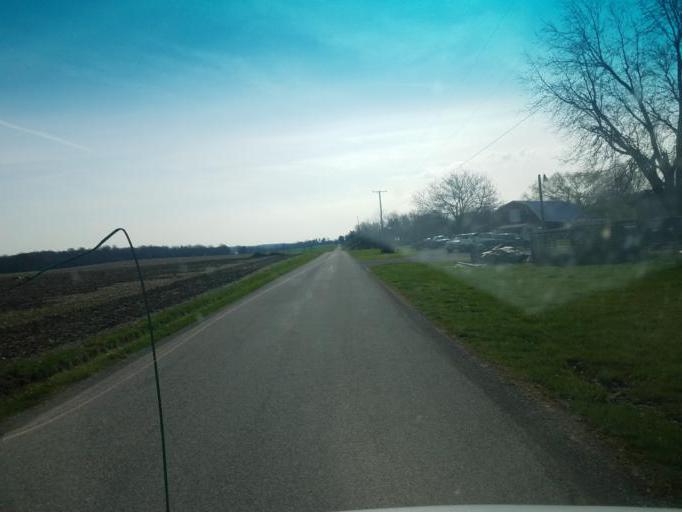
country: US
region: Ohio
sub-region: Richland County
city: Shelby
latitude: 40.8798
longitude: -82.5454
